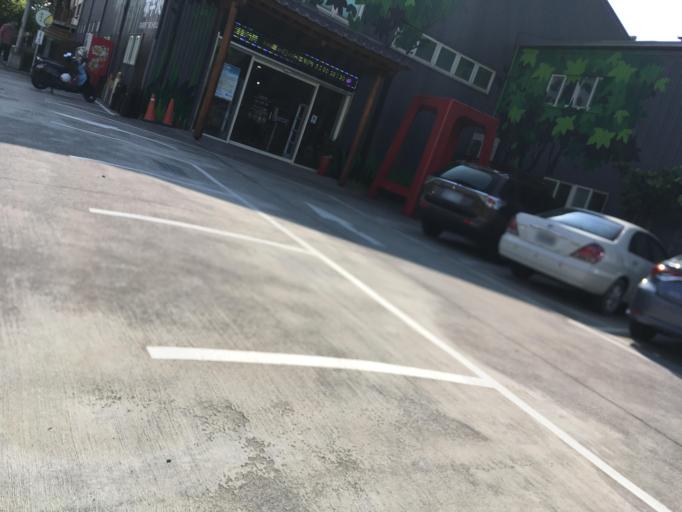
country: TW
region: Taiwan
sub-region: Yilan
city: Yilan
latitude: 24.6350
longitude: 121.8299
